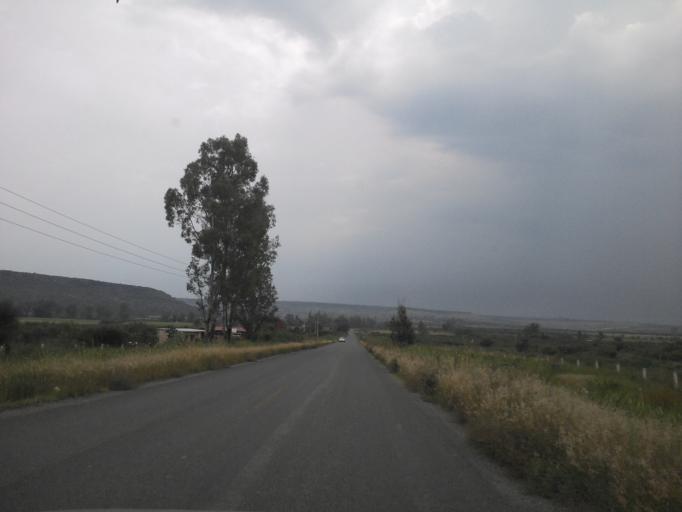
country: MX
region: Jalisco
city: San Diego de Alejandria
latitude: 20.8996
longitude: -102.0501
